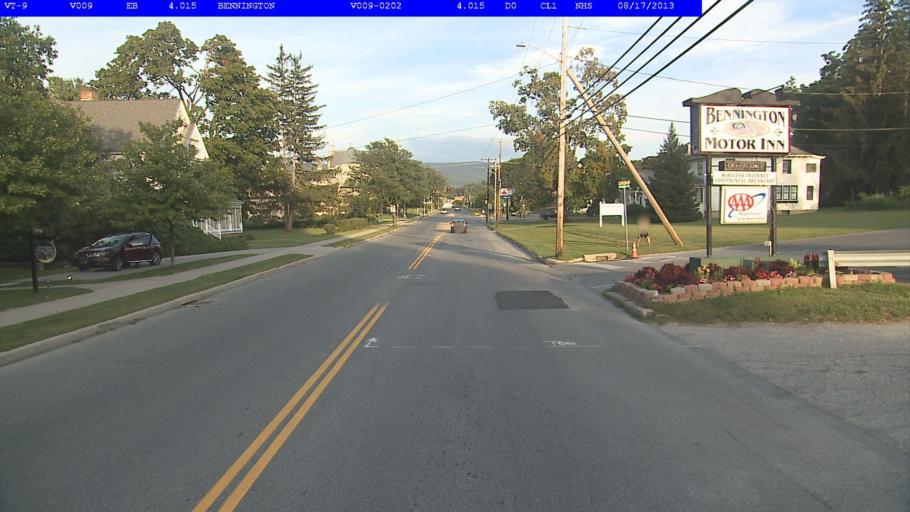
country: US
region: Vermont
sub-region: Bennington County
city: Bennington
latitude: 42.8811
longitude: -73.2036
